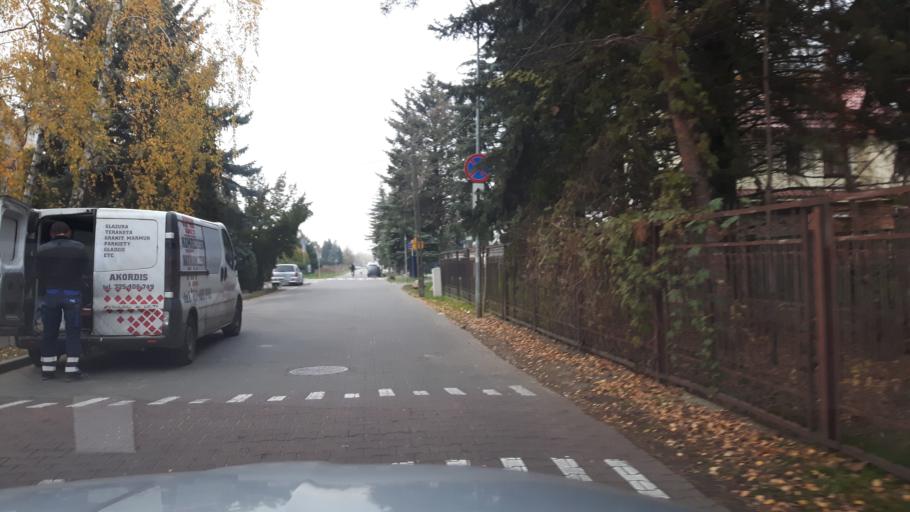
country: PL
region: Masovian Voivodeship
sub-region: Warszawa
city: Wilanow
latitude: 52.1719
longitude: 21.1133
